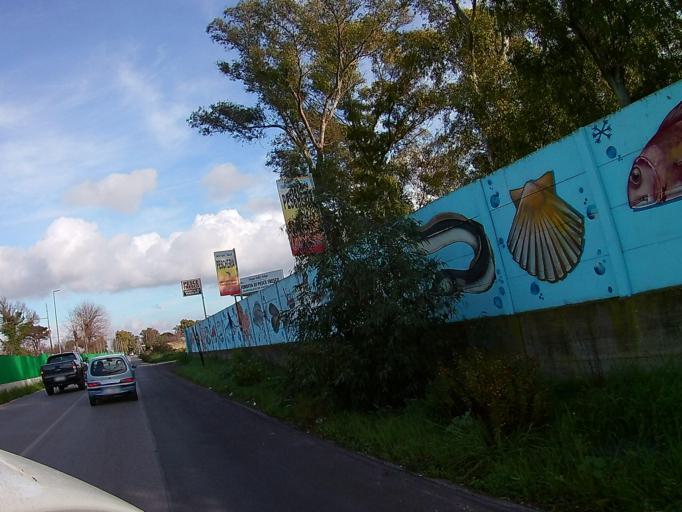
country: IT
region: Latium
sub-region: Citta metropolitana di Roma Capitale
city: Acilia-Castel Fusano-Ostia Antica
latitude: 41.7665
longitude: 12.3204
